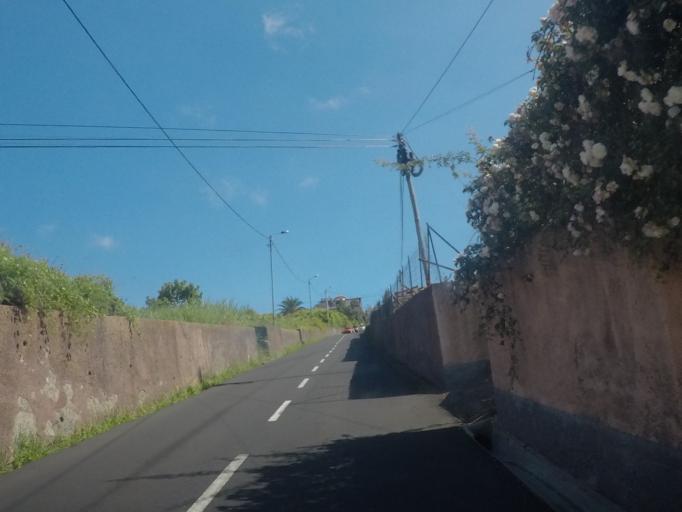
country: PT
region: Madeira
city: Camara de Lobos
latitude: 32.6694
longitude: -16.9653
